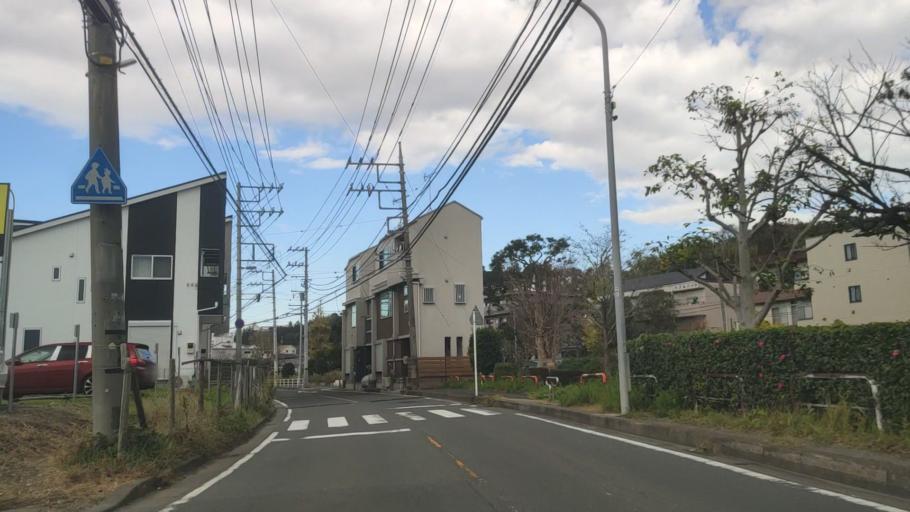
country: JP
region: Kanagawa
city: Minami-rinkan
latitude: 35.4261
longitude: 139.5290
